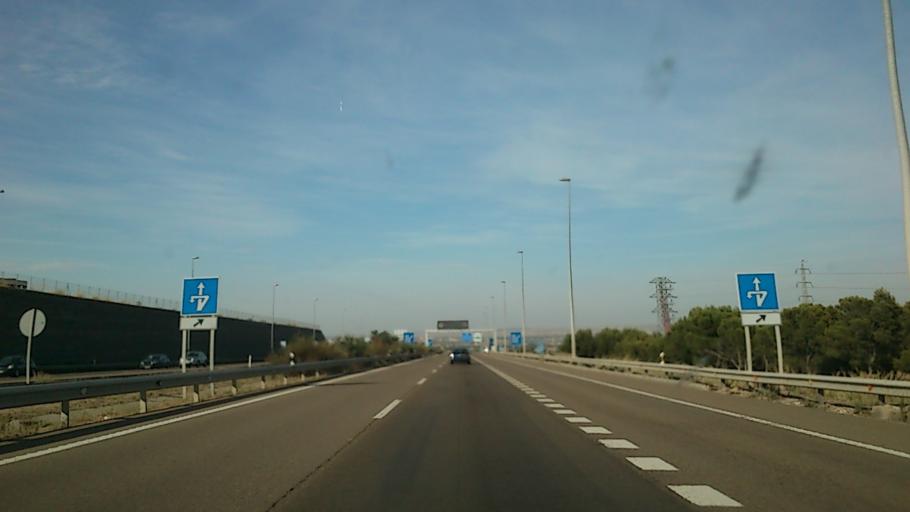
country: ES
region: Aragon
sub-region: Provincia de Zaragoza
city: Zaragoza
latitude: 41.6143
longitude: -0.8706
